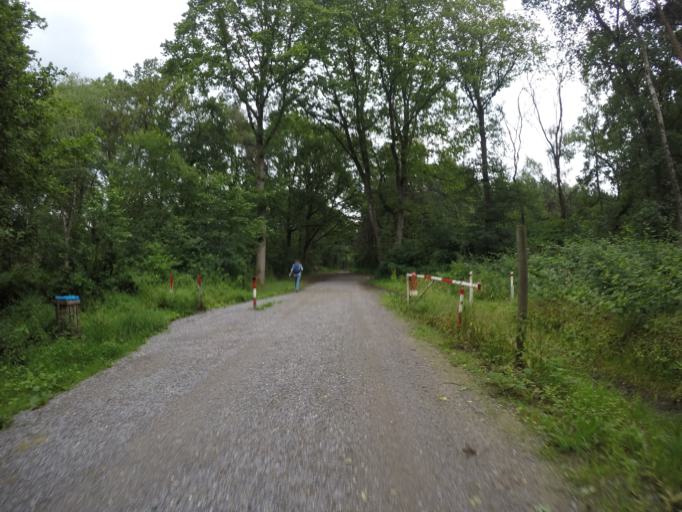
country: DE
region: North Rhine-Westphalia
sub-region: Regierungsbezirk Dusseldorf
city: Schermbeck
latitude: 51.5940
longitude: 6.8659
